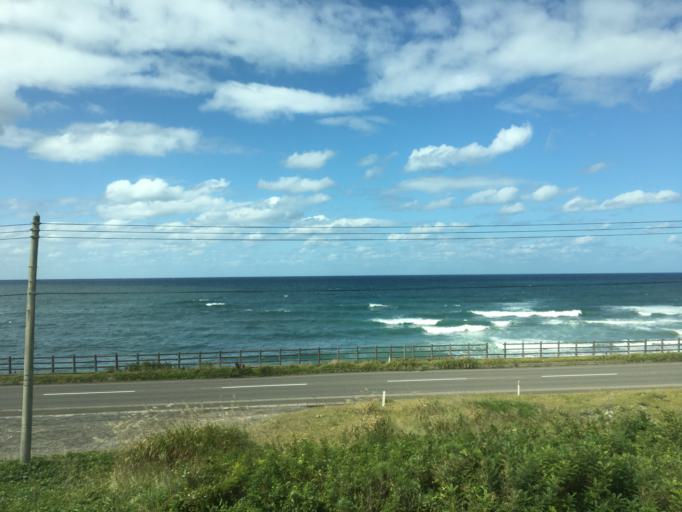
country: JP
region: Aomori
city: Shimokizukuri
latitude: 40.7677
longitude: 140.1680
